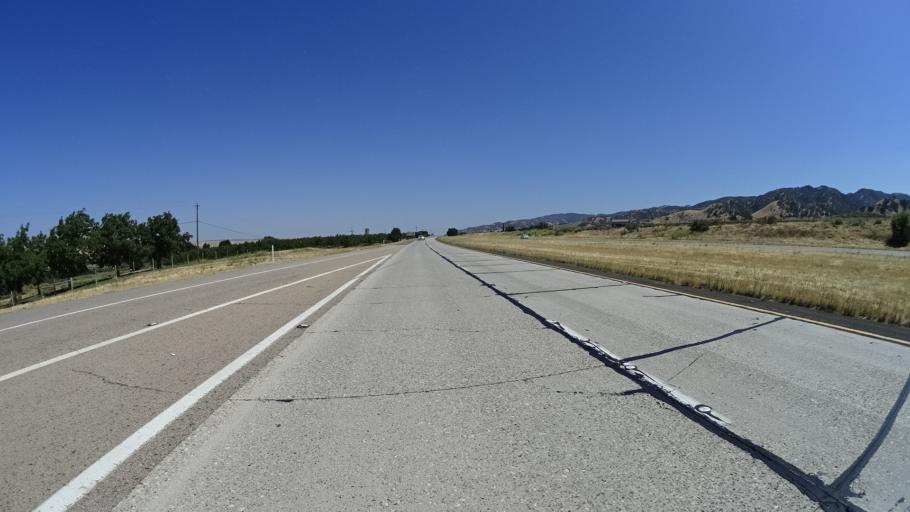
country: US
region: California
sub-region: San Luis Obispo County
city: Lake Nacimiento
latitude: 36.0100
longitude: -120.9197
